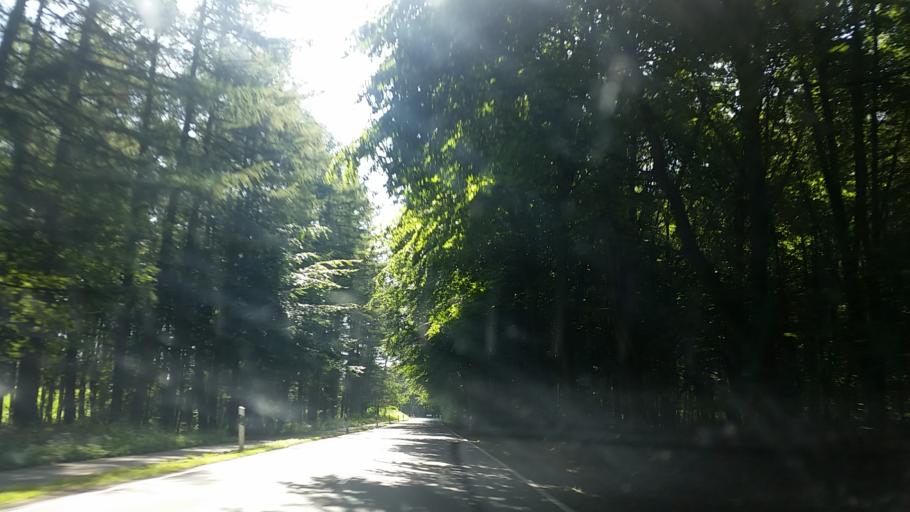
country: DE
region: Lower Saxony
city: Ankum
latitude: 52.5214
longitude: 7.8994
